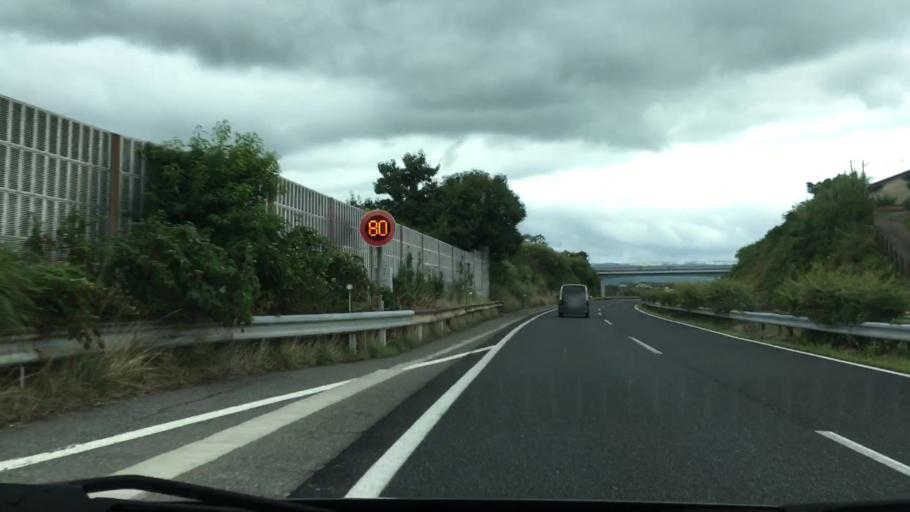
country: JP
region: Okayama
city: Tsuyama
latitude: 35.0648
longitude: 133.9849
